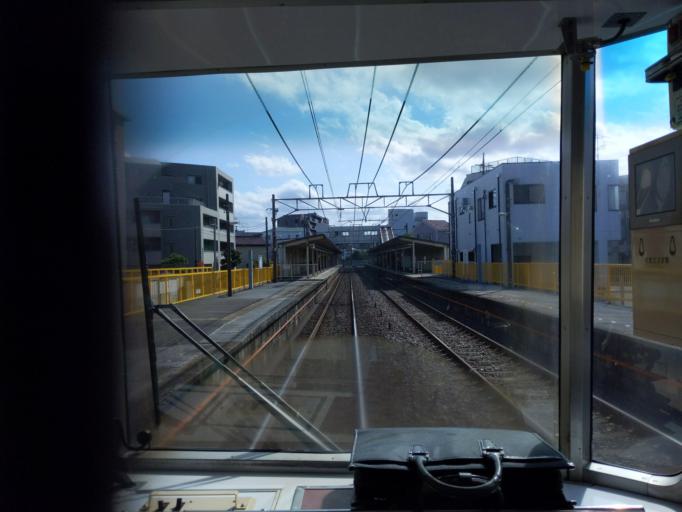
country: JP
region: Chiba
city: Funabashi
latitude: 35.7161
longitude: 140.0430
